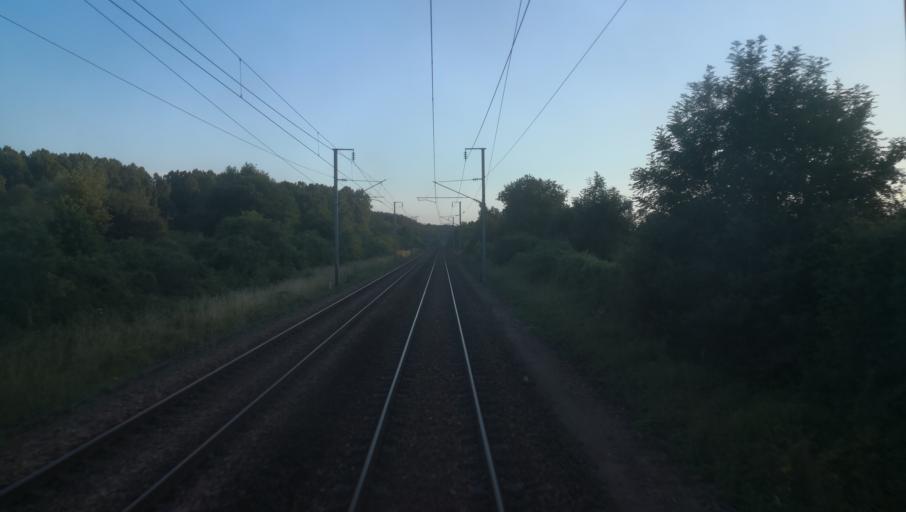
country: FR
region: Haute-Normandie
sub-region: Departement de l'Eure
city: Claville
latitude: 48.9848
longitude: 1.0274
